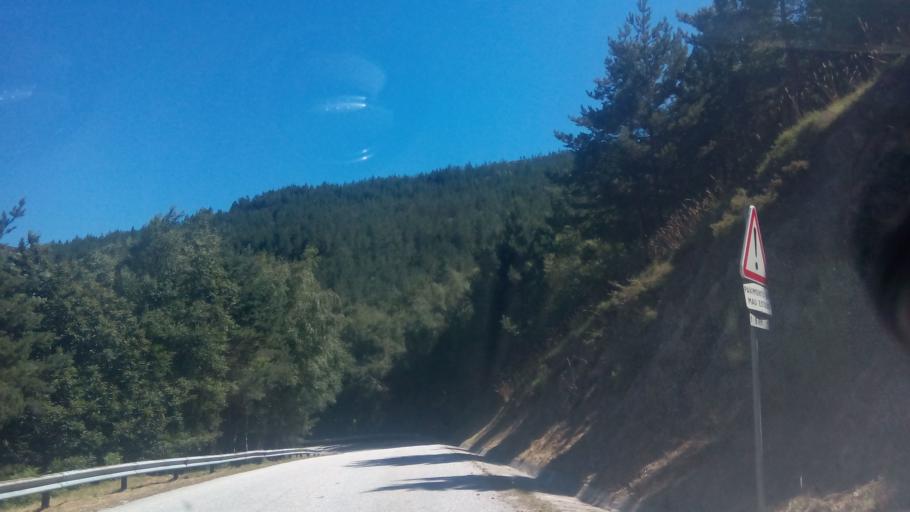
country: PT
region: Vila Real
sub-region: Mesao Frio
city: Mesao Frio
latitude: 41.2782
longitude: -7.9133
